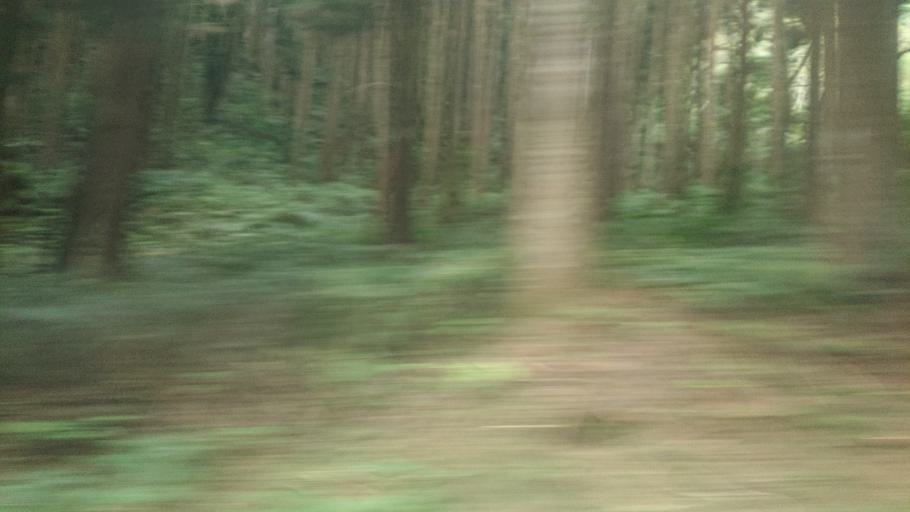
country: TW
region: Taiwan
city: Lugu
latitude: 23.5005
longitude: 120.7929
